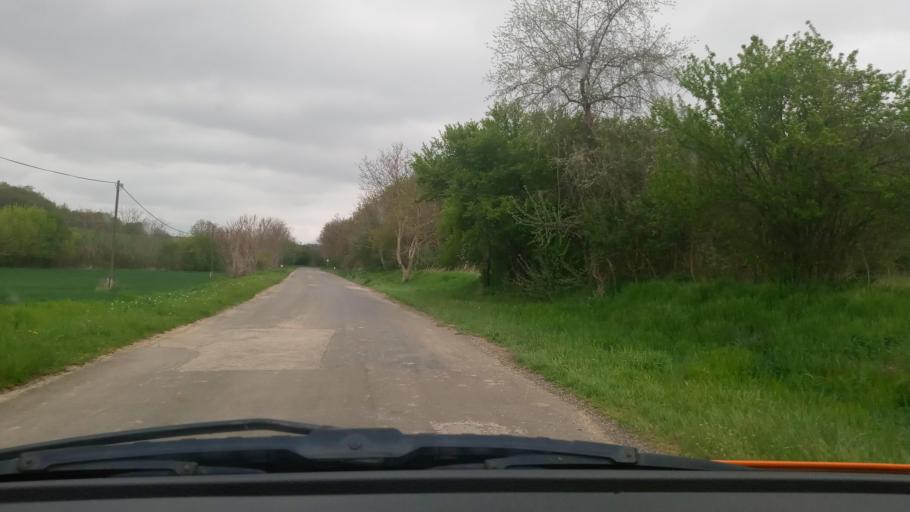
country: HU
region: Baranya
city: Boly
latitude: 46.0126
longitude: 18.5453
